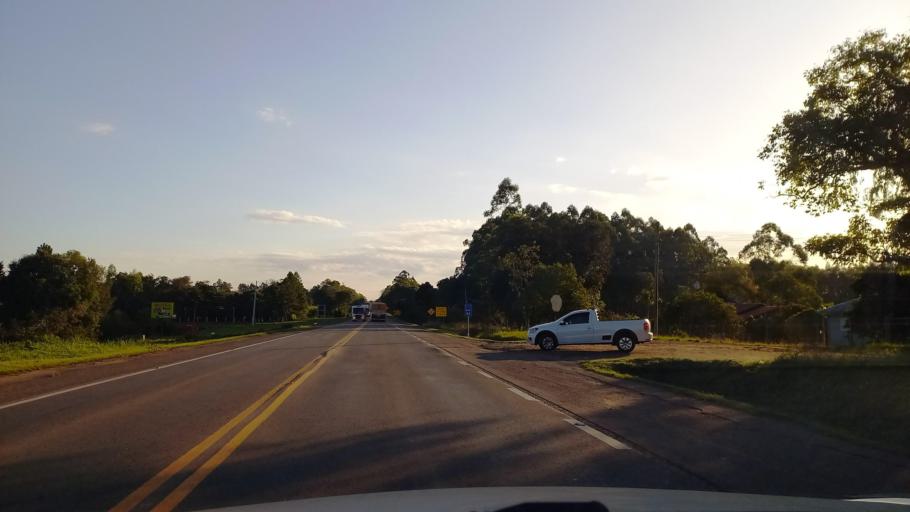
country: BR
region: Rio Grande do Sul
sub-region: Venancio Aires
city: Venancio Aires
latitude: -29.6574
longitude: -52.2329
